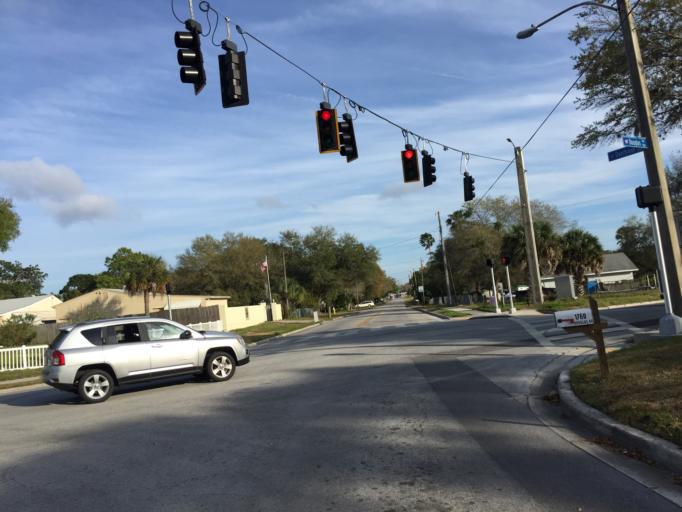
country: US
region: Florida
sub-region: Pinellas County
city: Clearwater
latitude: 27.9855
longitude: -82.7880
